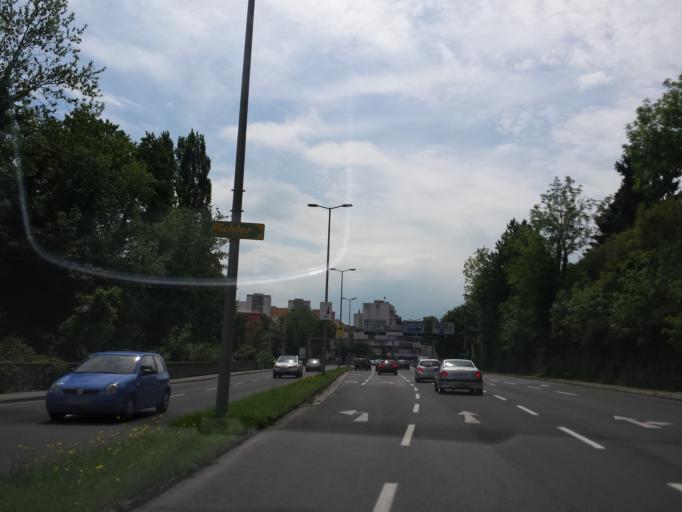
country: AT
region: Styria
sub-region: Graz Stadt
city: Goesting
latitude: 47.0844
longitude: 15.4146
